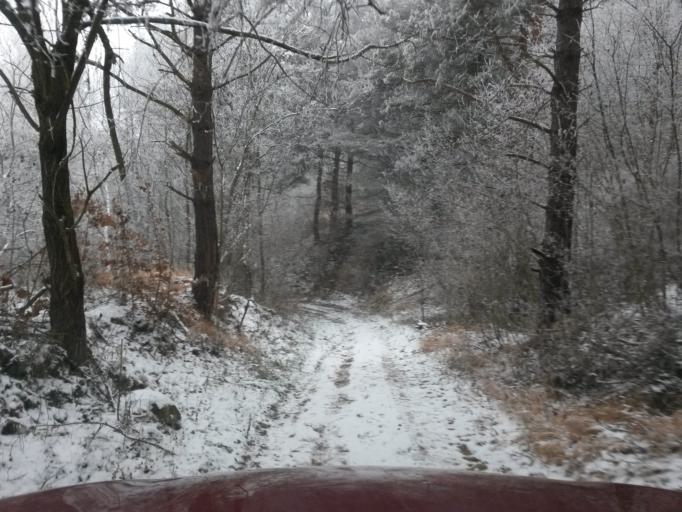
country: SK
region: Kosicky
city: Krompachy
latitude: 48.9713
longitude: 20.9797
